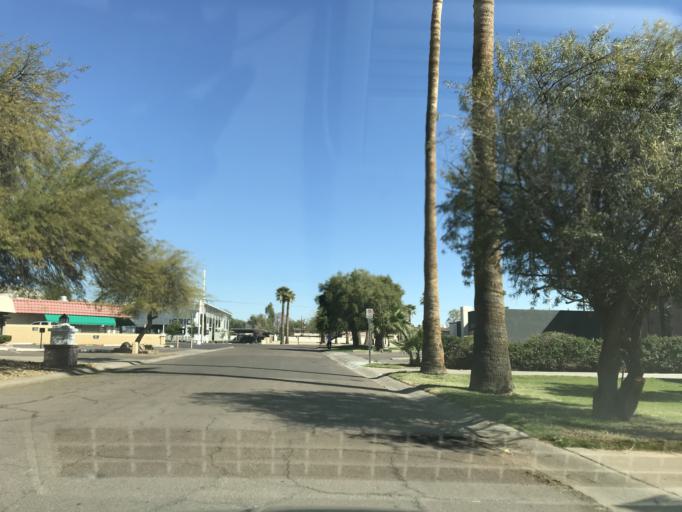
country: US
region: Arizona
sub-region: Maricopa County
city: Phoenix
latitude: 33.5137
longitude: -112.0661
